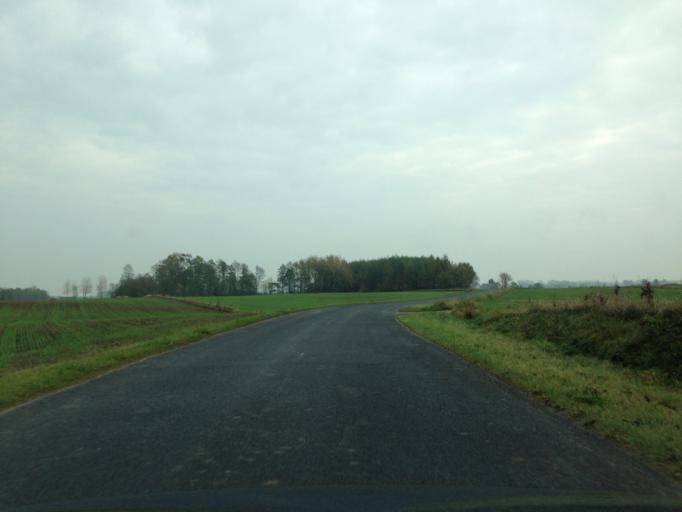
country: PL
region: Kujawsko-Pomorskie
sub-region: Powiat rypinski
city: Rypin
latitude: 53.1249
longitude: 19.4646
